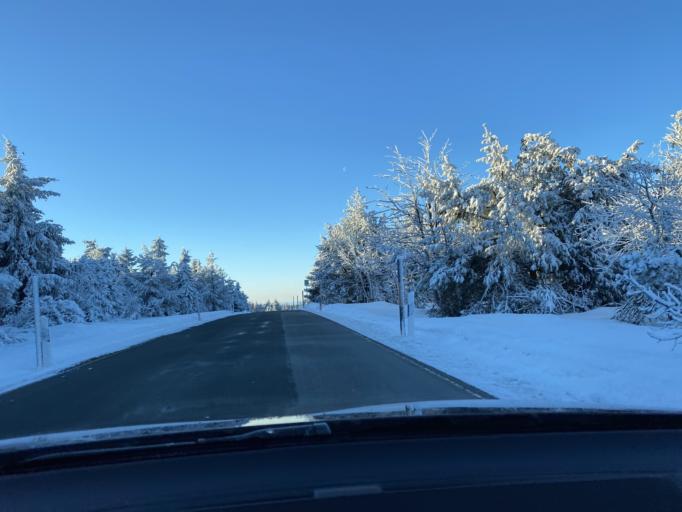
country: DE
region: Saxony
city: Kurort Oberwiesenthal
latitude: 50.4173
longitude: 12.9369
